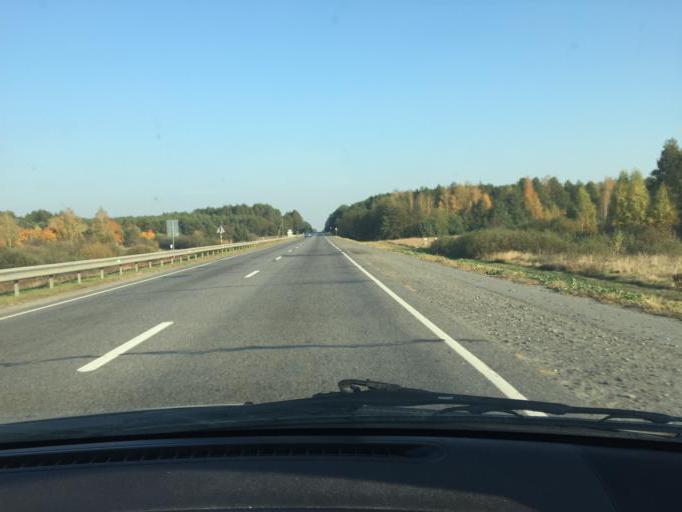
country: BY
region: Brest
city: Davyd-Haradok
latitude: 52.2475
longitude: 27.0898
